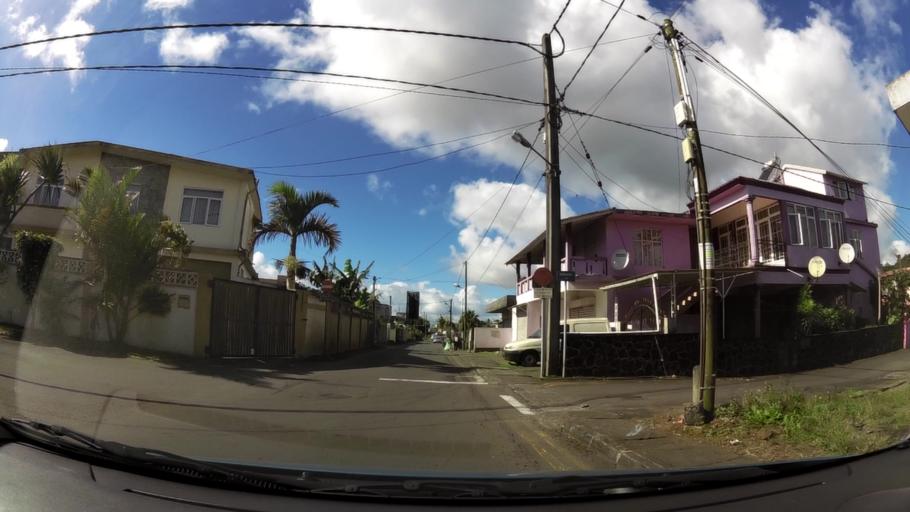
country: MU
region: Plaines Wilhems
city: Curepipe
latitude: -20.3246
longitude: 57.5332
